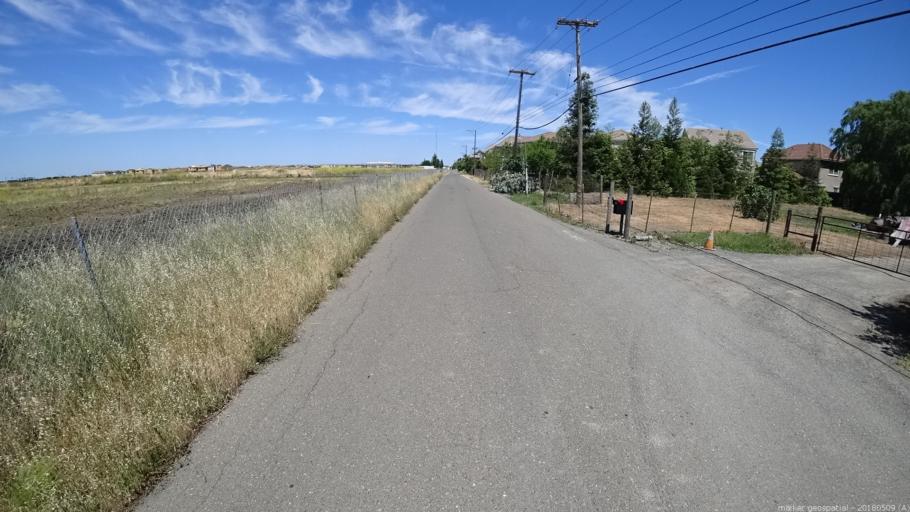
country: US
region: California
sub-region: Yolo County
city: West Sacramento
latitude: 38.6337
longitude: -121.5142
